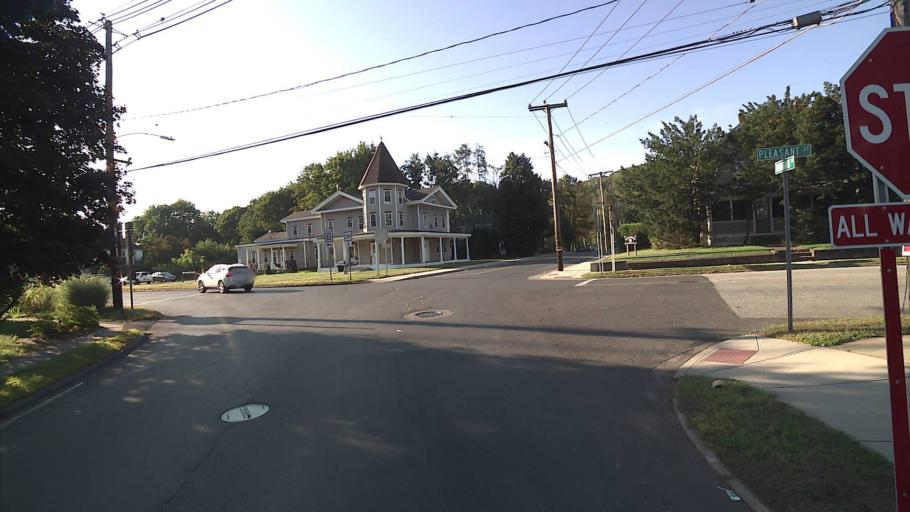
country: US
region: Connecticut
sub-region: Windham County
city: Willimantic
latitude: 41.7100
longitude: -72.2187
